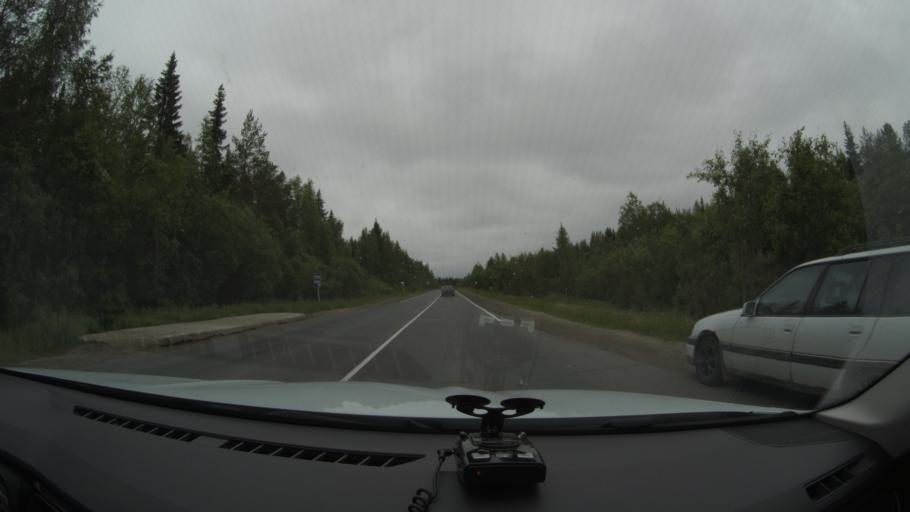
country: RU
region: Komi Republic
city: Shudayag
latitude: 63.5553
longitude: 53.5117
